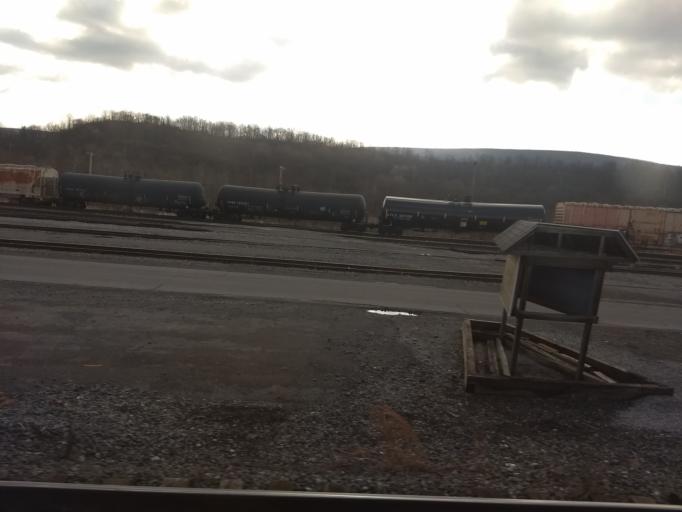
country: US
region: Pennsylvania
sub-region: Blair County
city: Greenwood
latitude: 40.5412
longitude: -78.3762
